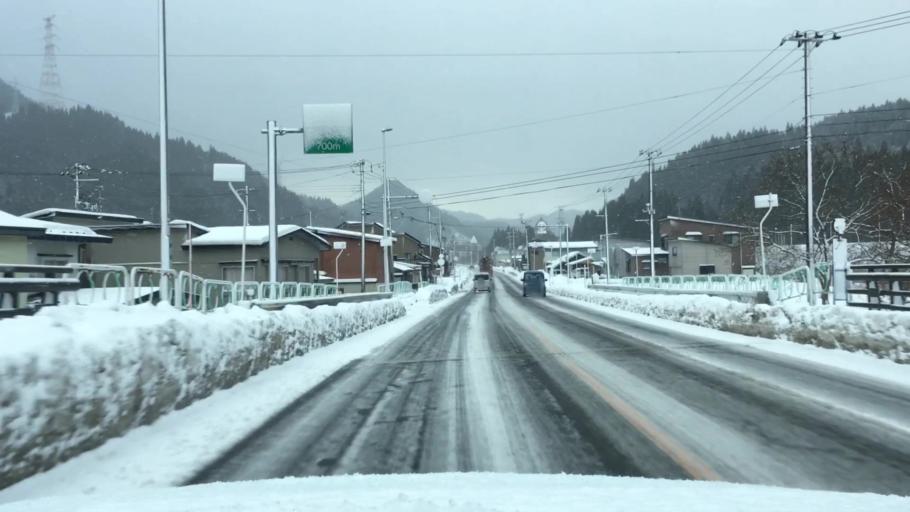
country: JP
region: Aomori
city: Kuroishi
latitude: 40.4697
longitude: 140.6329
